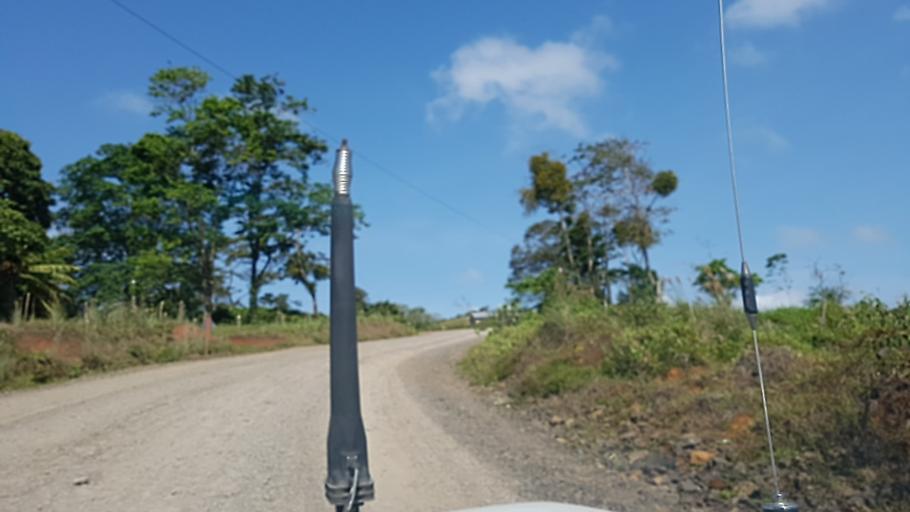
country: NI
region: Atlantico Sur
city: Nueva Guinea
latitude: 11.7880
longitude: -84.1639
